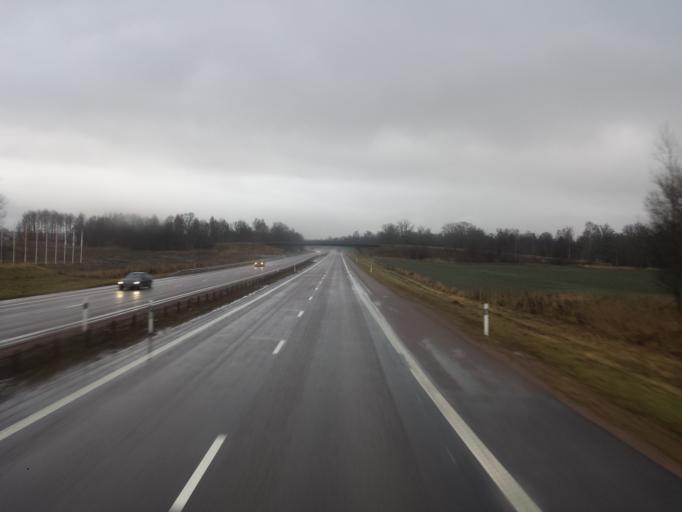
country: SE
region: OEstergoetland
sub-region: Odeshogs Kommun
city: OEdeshoeg
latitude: 58.2302
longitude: 14.6816
